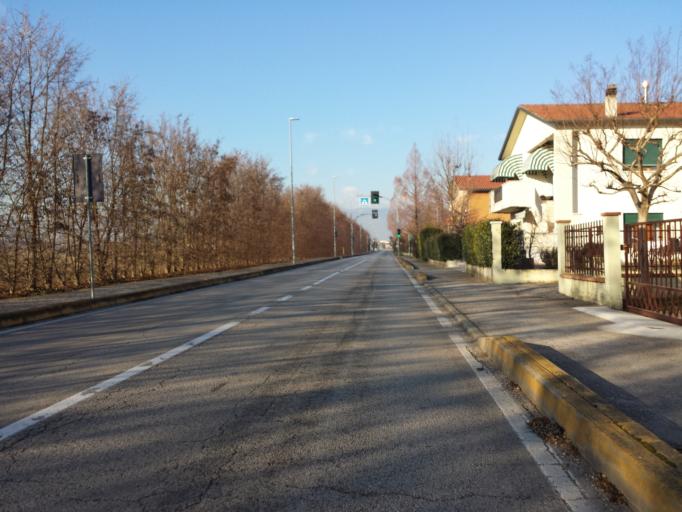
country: IT
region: Veneto
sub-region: Provincia di Vicenza
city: Poianella
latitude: 45.6430
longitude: 11.6077
